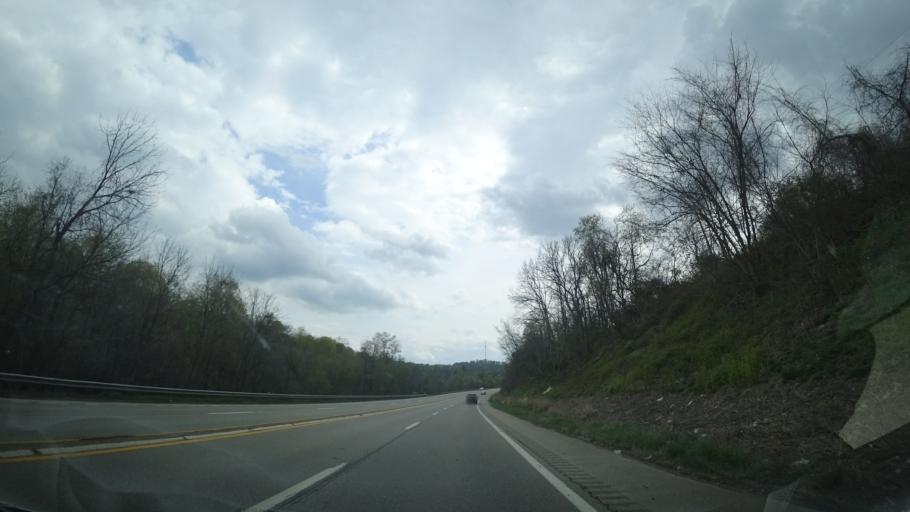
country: US
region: Pennsylvania
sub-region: Fayette County
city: Perryopolis
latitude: 40.0330
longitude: -79.7701
